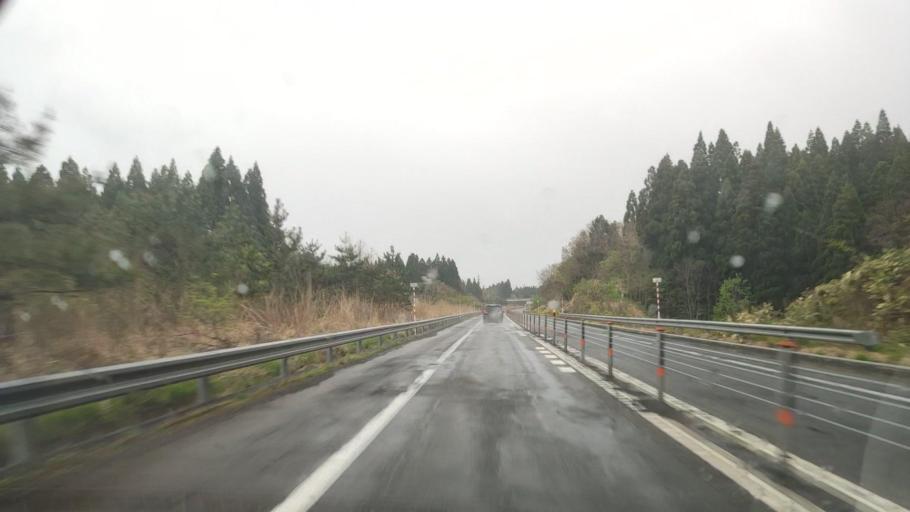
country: JP
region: Akita
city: Noshiromachi
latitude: 40.1718
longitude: 140.0535
